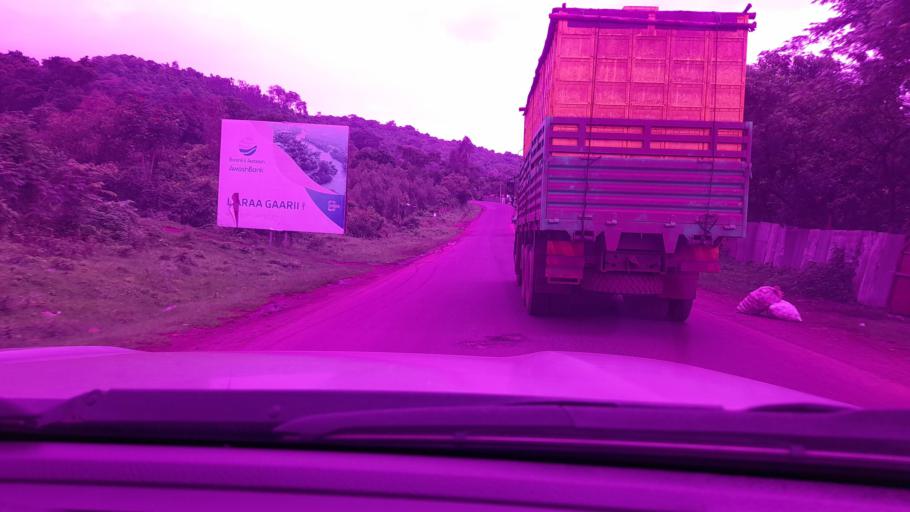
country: ET
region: Oromiya
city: Jima
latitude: 7.6600
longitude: 36.8789
